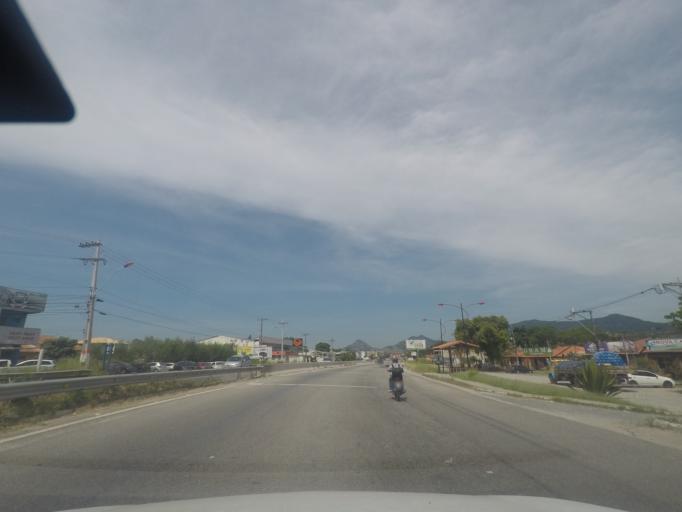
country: BR
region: Rio de Janeiro
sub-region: Marica
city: Marica
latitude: -22.9072
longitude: -42.8192
